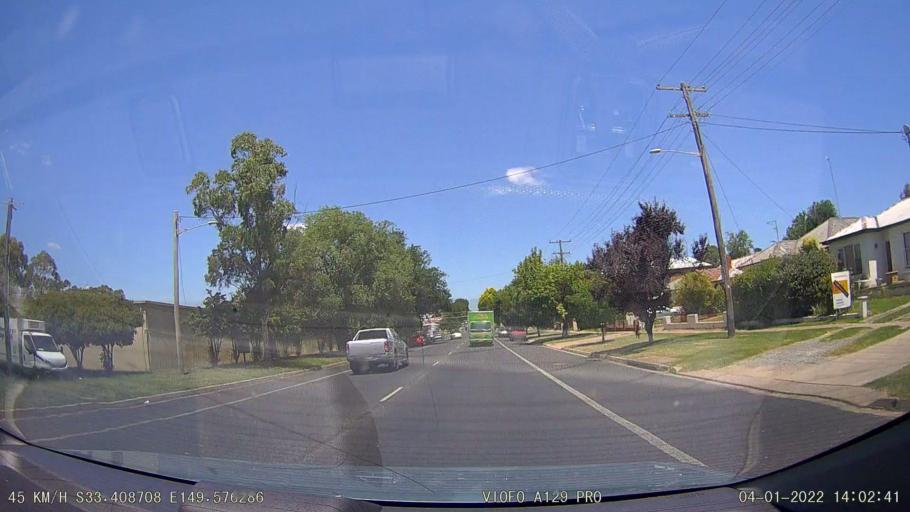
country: AU
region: New South Wales
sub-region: Bathurst Regional
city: Bathurst
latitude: -33.4086
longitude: 149.5762
